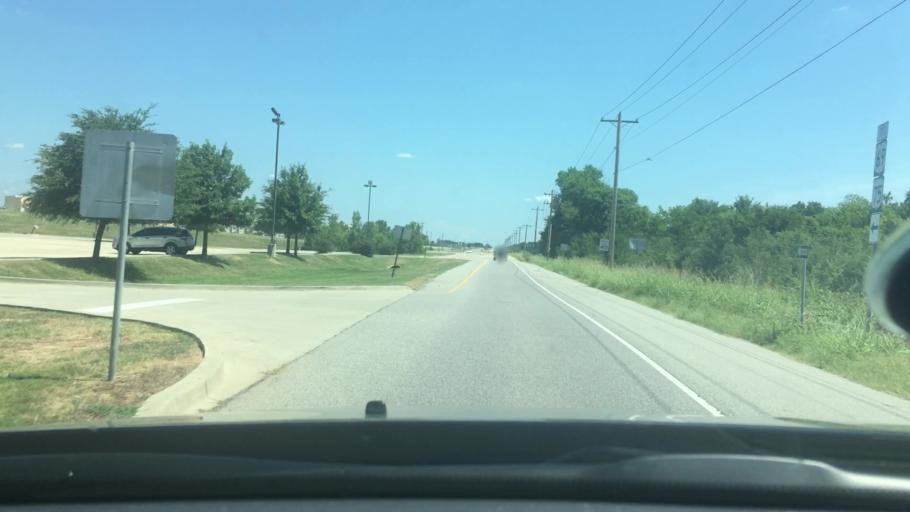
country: US
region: Oklahoma
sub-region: Bryan County
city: Calera
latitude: 33.9440
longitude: -96.4162
